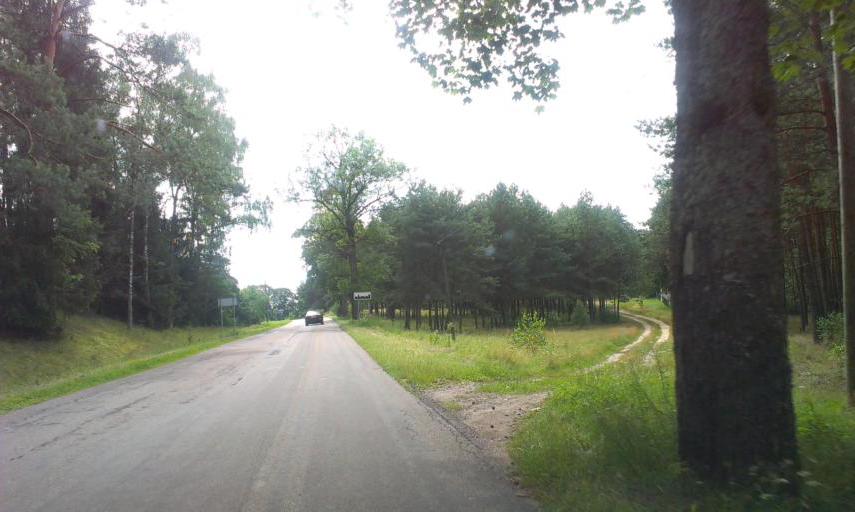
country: PL
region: West Pomeranian Voivodeship
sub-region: Powiat szczecinecki
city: Barwice
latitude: 53.6546
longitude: 16.3192
